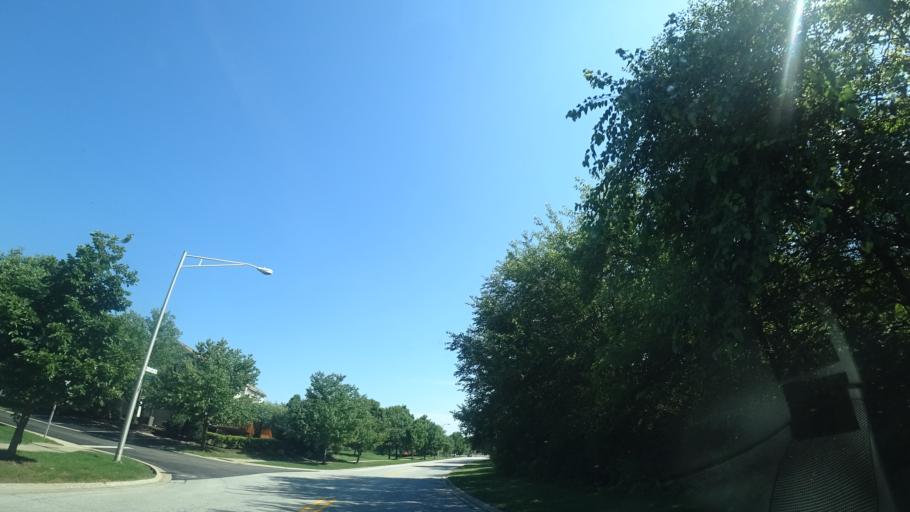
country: US
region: Illinois
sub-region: Will County
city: Mokena
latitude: 41.5629
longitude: -87.9093
